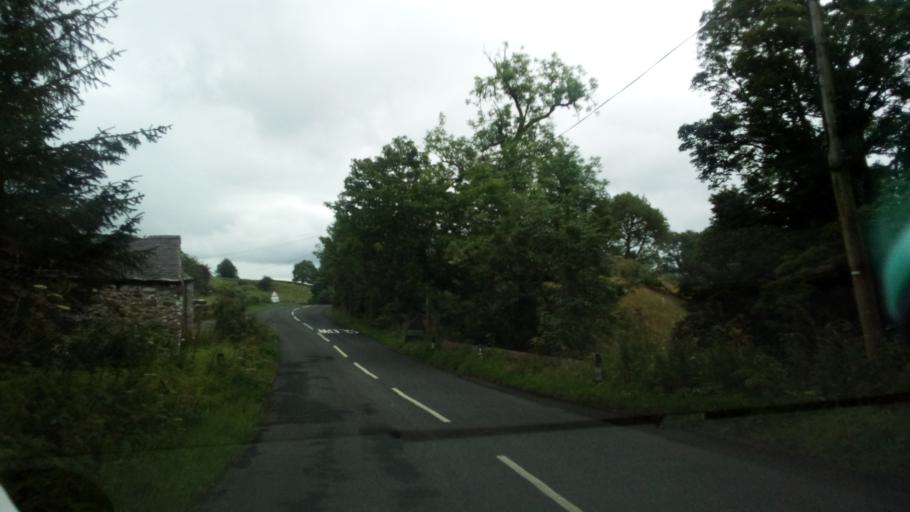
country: GB
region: England
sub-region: County Durham
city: Mickleton
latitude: 54.6082
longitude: -2.0860
